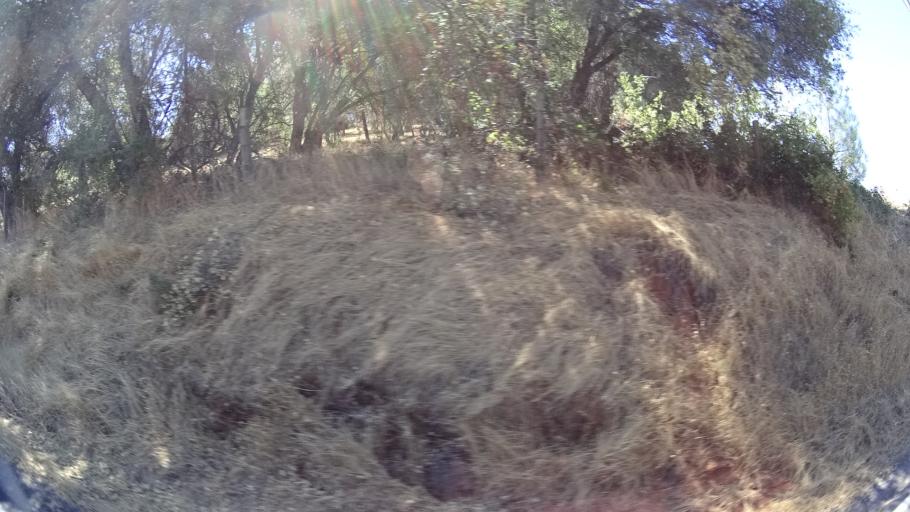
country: US
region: California
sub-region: Calaveras County
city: San Andreas
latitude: 38.1897
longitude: -120.6491
